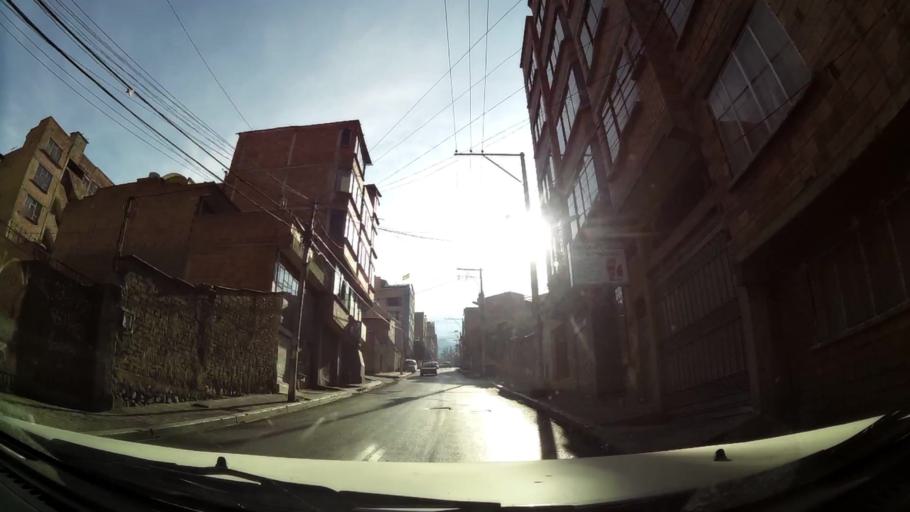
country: BO
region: La Paz
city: La Paz
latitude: -16.4931
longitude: -68.1160
